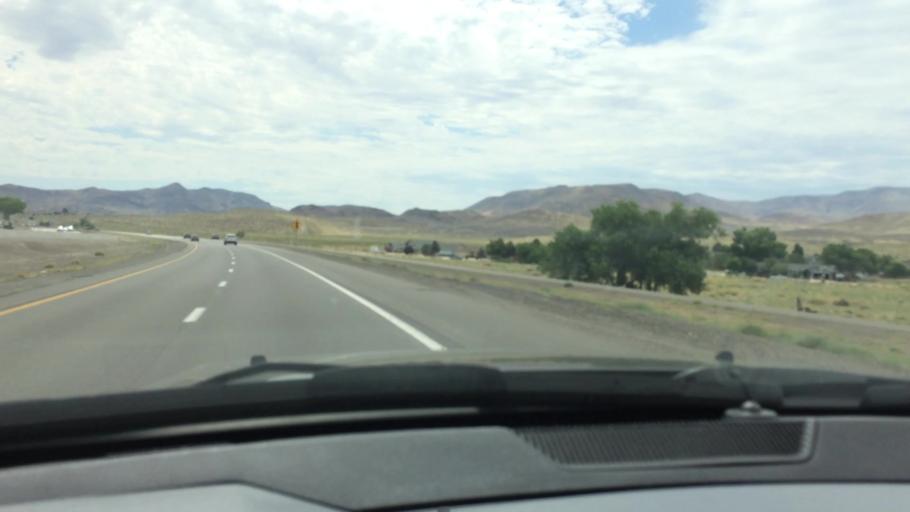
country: US
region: Nevada
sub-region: Lyon County
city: Fernley
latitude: 39.6164
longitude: -119.3090
